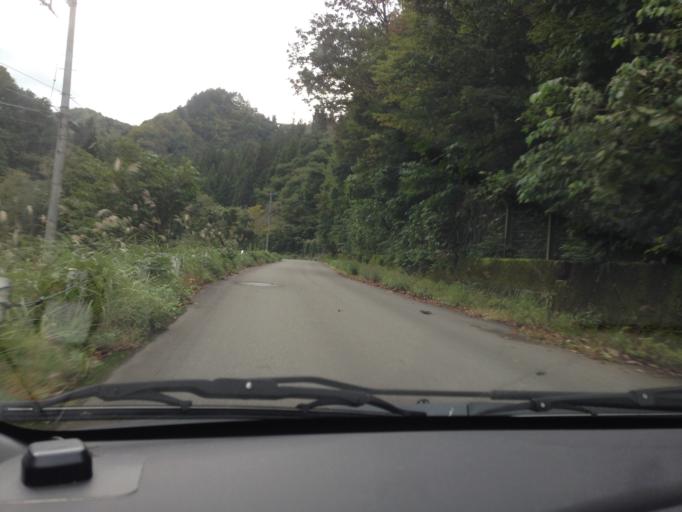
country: JP
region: Fukushima
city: Kitakata
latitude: 37.4145
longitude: 139.6299
